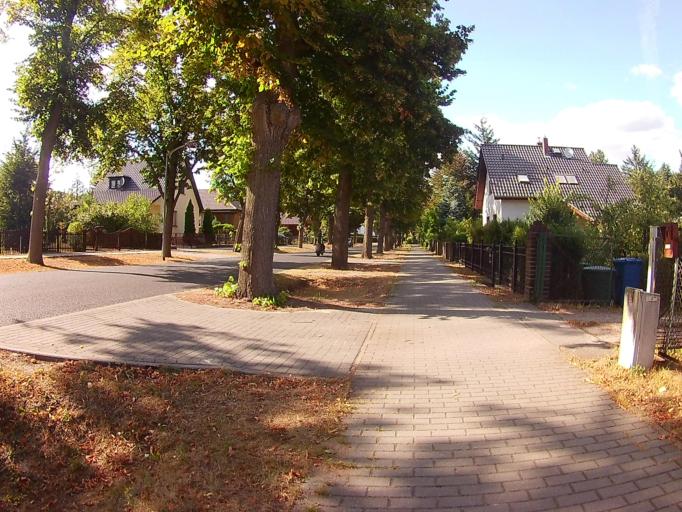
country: DE
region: Brandenburg
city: Schulzendorf
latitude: 52.3772
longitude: 13.5988
